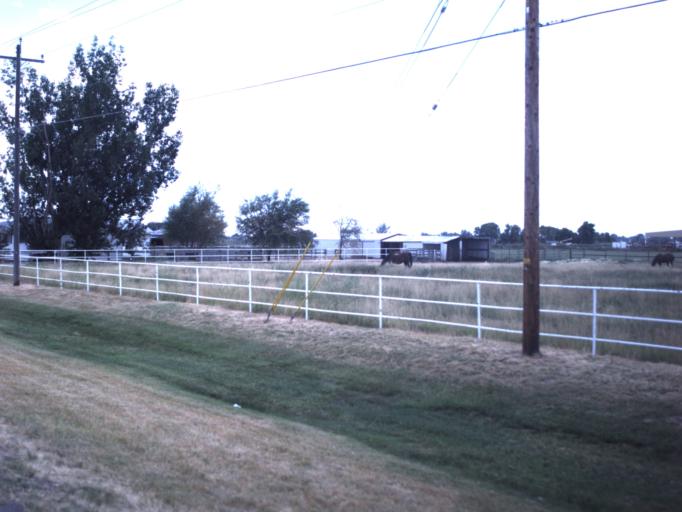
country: US
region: Utah
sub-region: Weber County
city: Hooper
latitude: 41.1399
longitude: -112.1133
